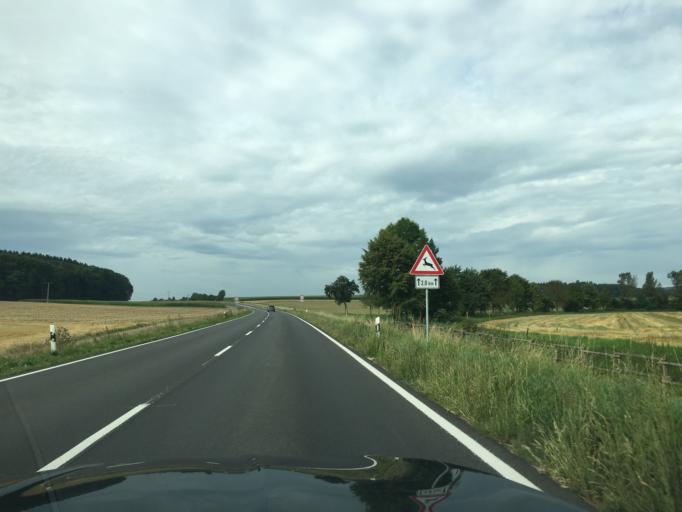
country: DE
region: Baden-Wuerttemberg
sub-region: Tuebingen Region
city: Obermarchtal
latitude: 48.2301
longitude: 9.5599
